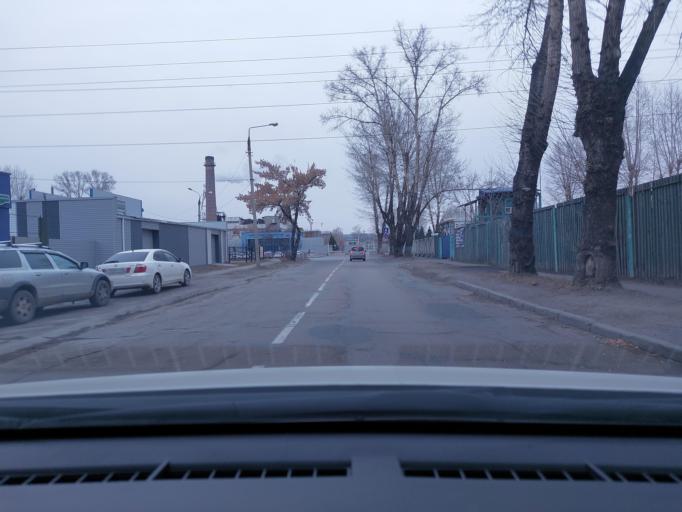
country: RU
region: Irkutsk
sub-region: Irkutskiy Rayon
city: Irkutsk
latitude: 52.3425
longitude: 104.2283
